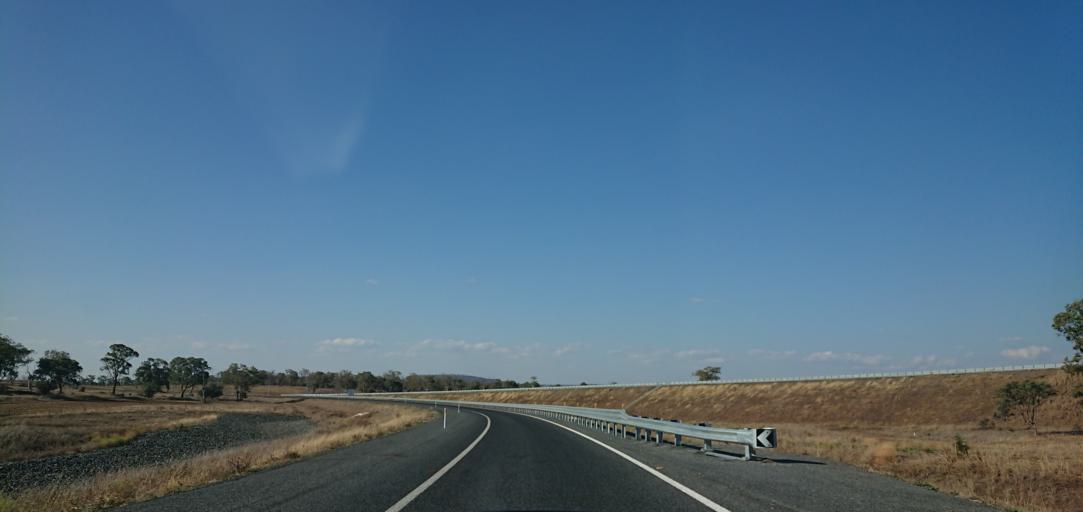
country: AU
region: Queensland
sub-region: Toowoomba
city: Westbrook
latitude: -27.6146
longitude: 151.7846
